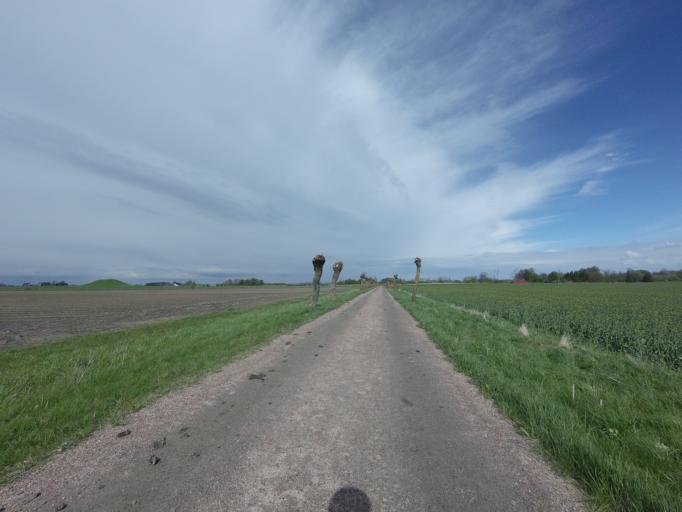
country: SE
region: Skane
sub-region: Malmo
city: Bunkeflostrand
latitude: 55.5404
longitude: 12.9719
